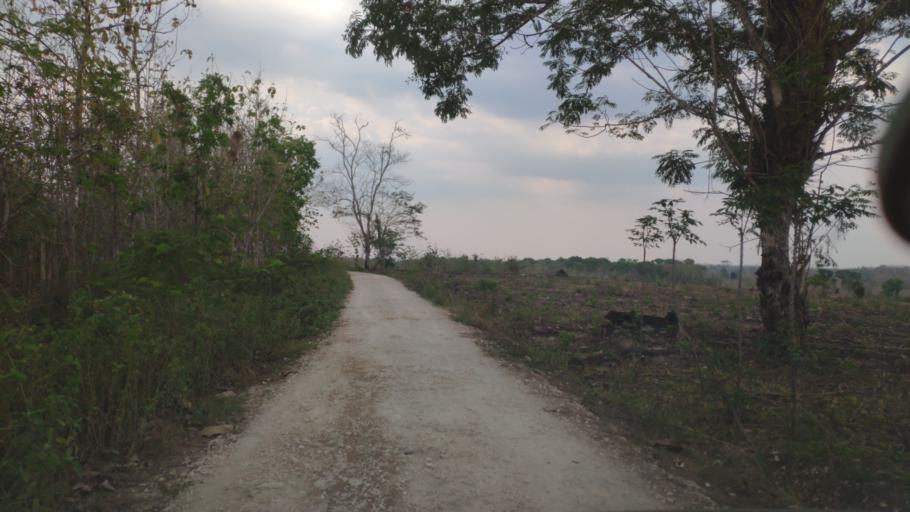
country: ID
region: Central Java
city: Randublatung
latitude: -7.2849
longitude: 111.2947
